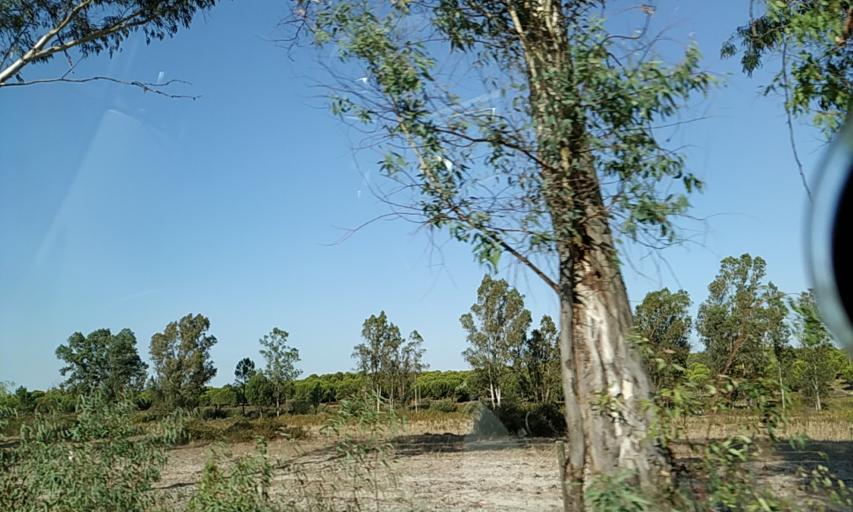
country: PT
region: Santarem
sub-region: Coruche
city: Coruche
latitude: 39.0104
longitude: -8.5627
